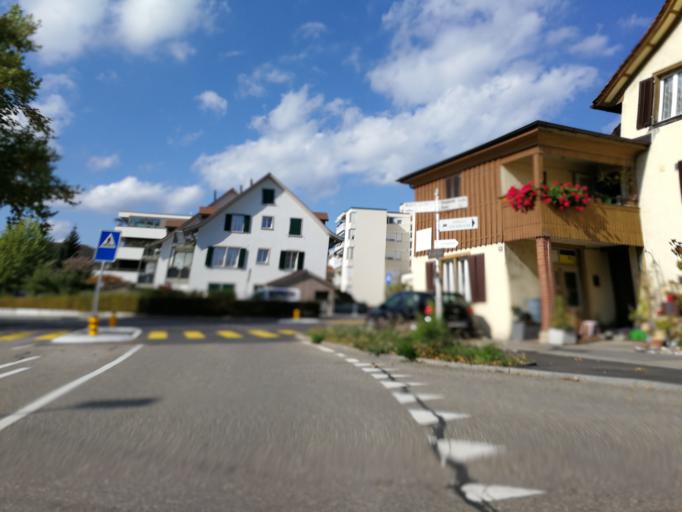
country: CH
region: Zurich
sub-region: Bezirk Meilen
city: Uetikon / Grossdorf
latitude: 47.2666
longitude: 8.6761
